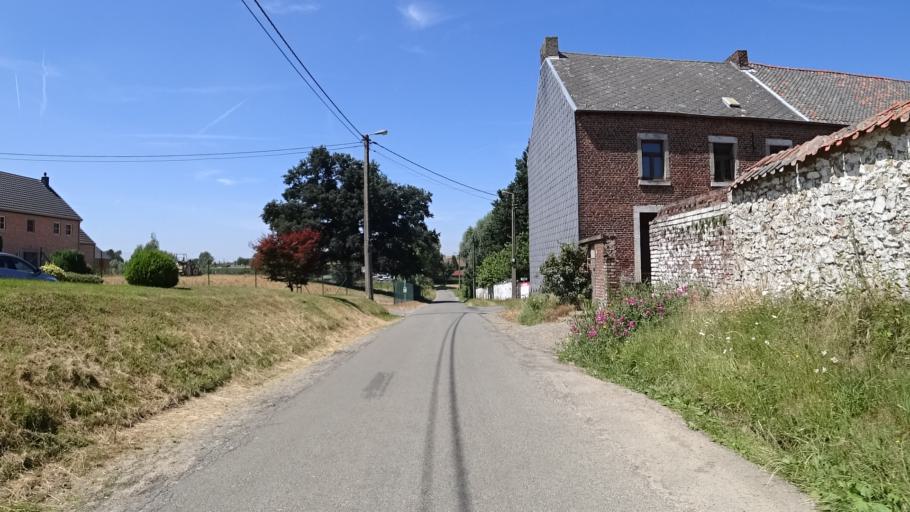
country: BE
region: Wallonia
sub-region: Province du Brabant Wallon
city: Incourt
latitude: 50.6691
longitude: 4.8331
